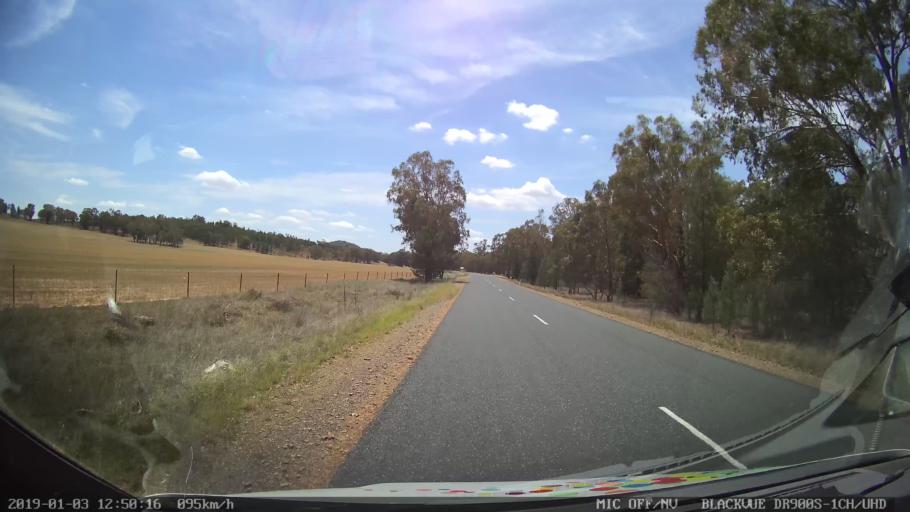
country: AU
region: New South Wales
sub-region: Weddin
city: Grenfell
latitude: -33.6933
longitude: 148.2684
